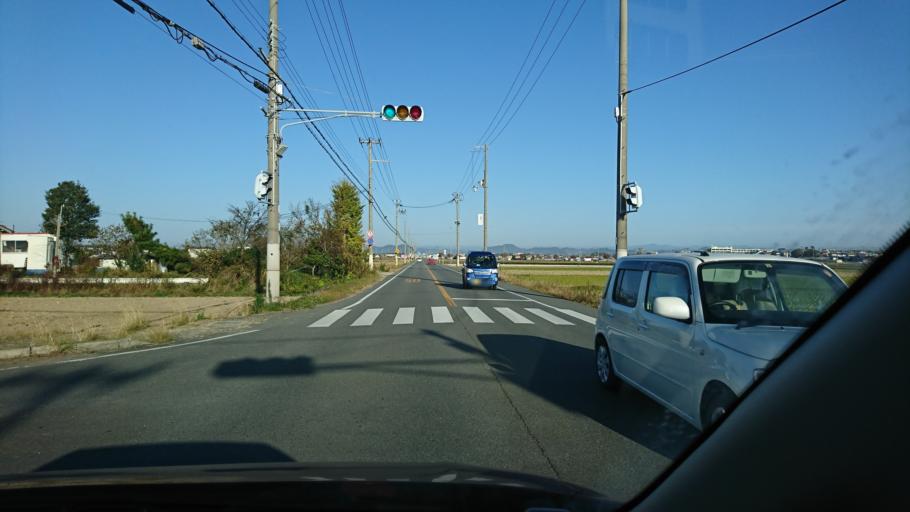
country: JP
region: Hyogo
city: Kakogawacho-honmachi
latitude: 34.7392
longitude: 134.9036
